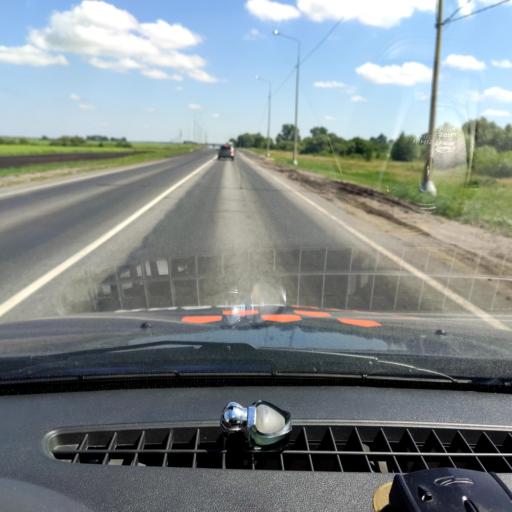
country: RU
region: Orjol
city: Zmiyevka
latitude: 52.7010
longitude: 36.3744
